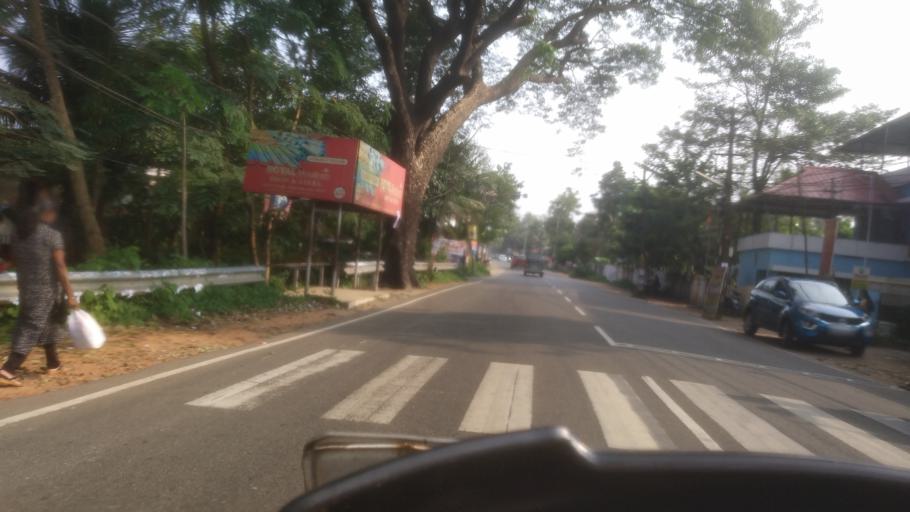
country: IN
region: Kerala
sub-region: Alappuzha
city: Arukutti
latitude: 9.8979
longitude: 76.3693
